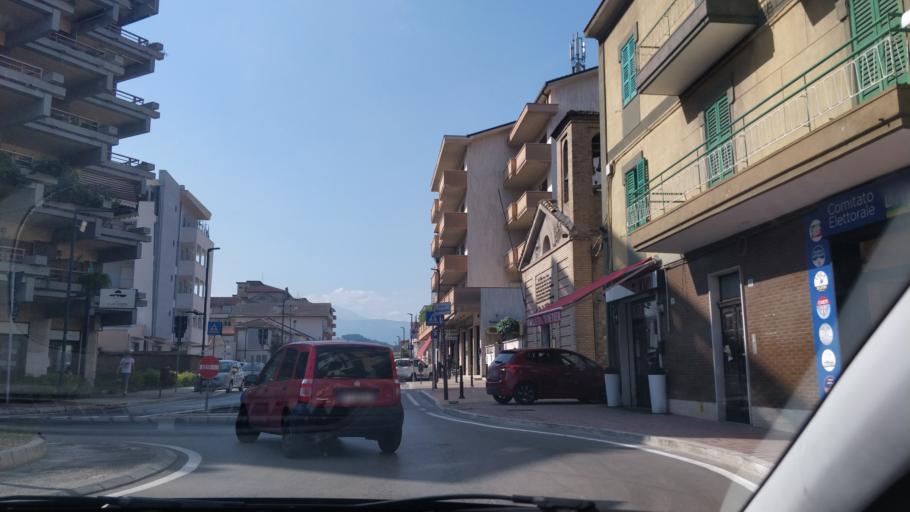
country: IT
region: Abruzzo
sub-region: Provincia di Chieti
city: Chieti
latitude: 42.3550
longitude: 14.1382
